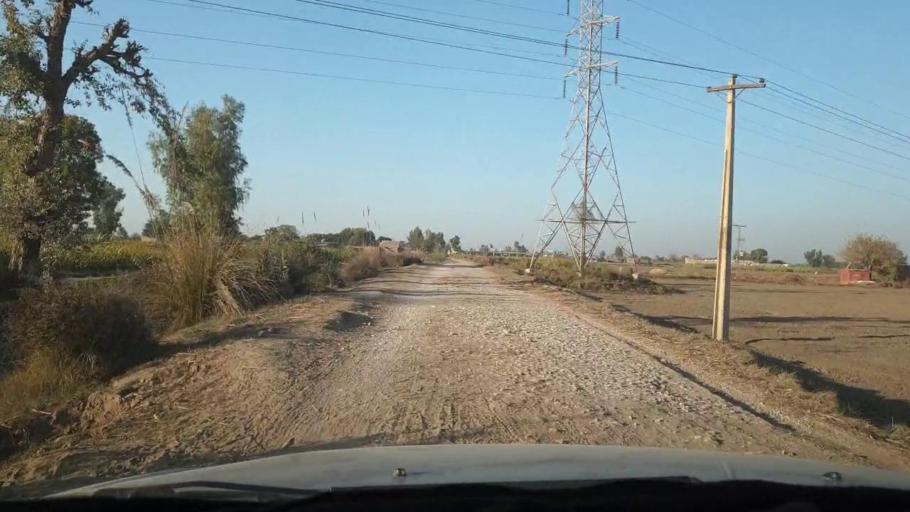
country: PK
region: Sindh
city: Ghotki
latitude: 27.9907
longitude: 69.2727
